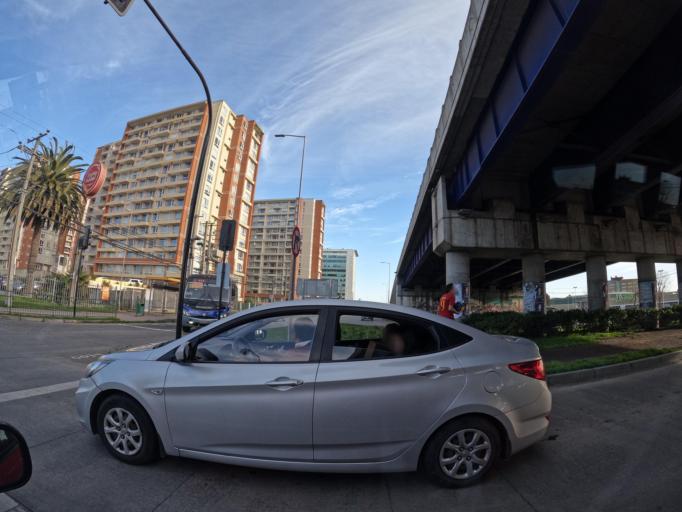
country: CL
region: Biobio
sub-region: Provincia de Concepcion
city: Concepcion
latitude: -36.7903
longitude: -73.0619
